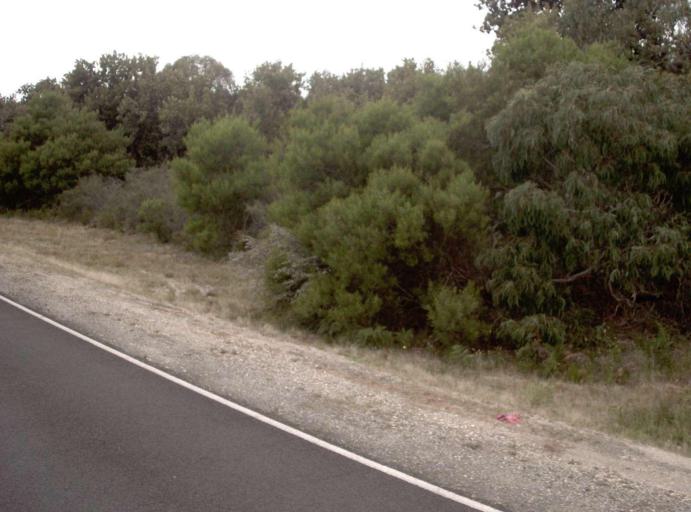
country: AU
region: Victoria
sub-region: East Gippsland
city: Bairnsdale
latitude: -38.0869
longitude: 147.5239
